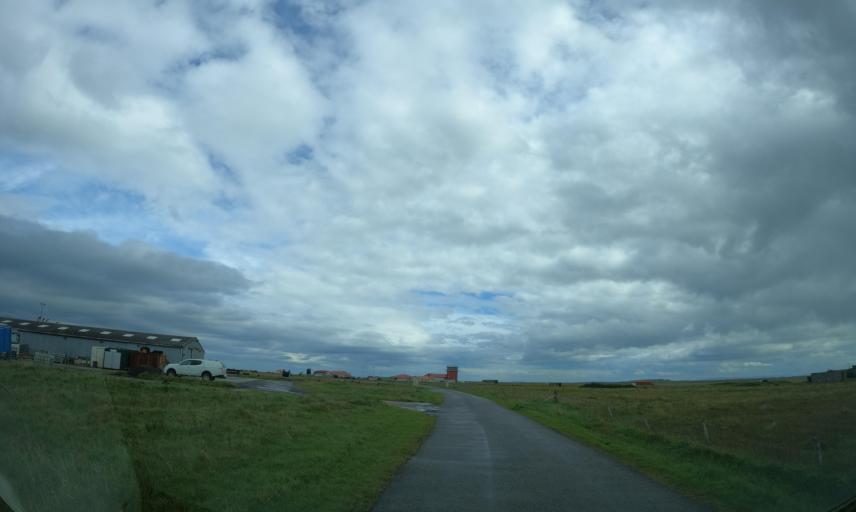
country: GB
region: Scotland
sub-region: Eilean Siar
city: Barra
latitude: 56.4969
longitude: -6.8806
